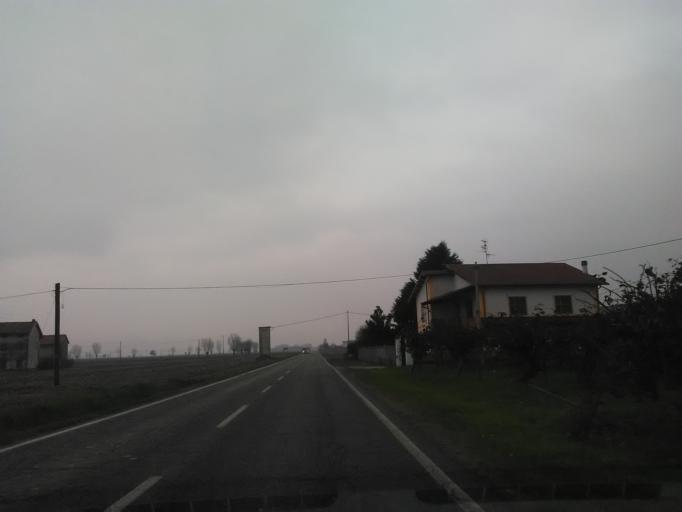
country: IT
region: Piedmont
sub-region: Provincia di Vercelli
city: Tronzano Vercellese
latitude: 45.3384
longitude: 8.1588
